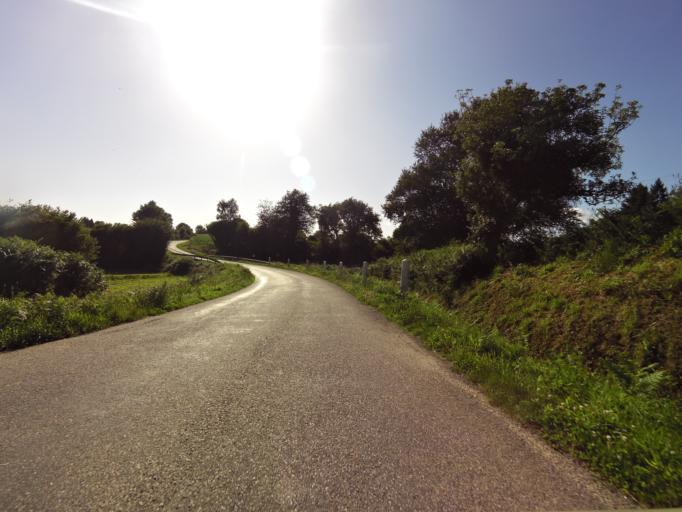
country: FR
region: Brittany
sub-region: Departement du Morbihan
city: Caden
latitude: 47.6264
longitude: -2.3201
